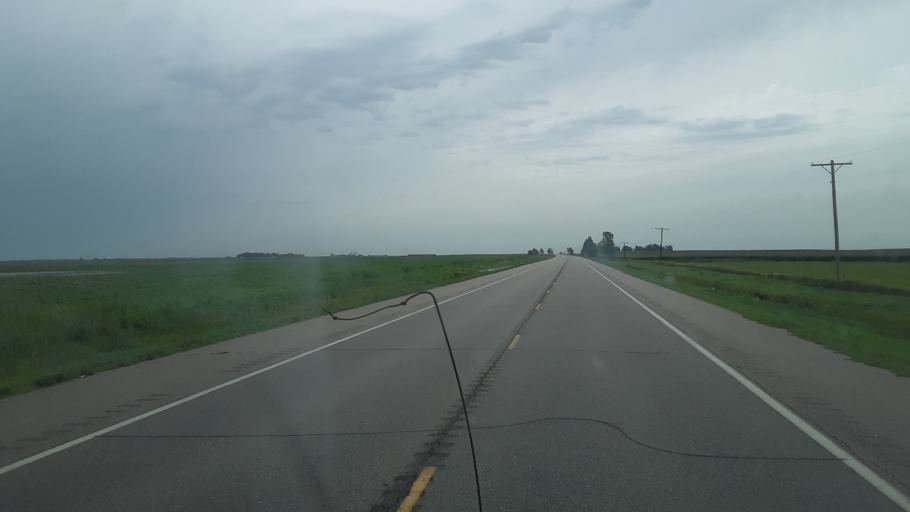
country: US
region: Kansas
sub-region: Stafford County
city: Saint John
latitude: 37.9564
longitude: -98.9495
